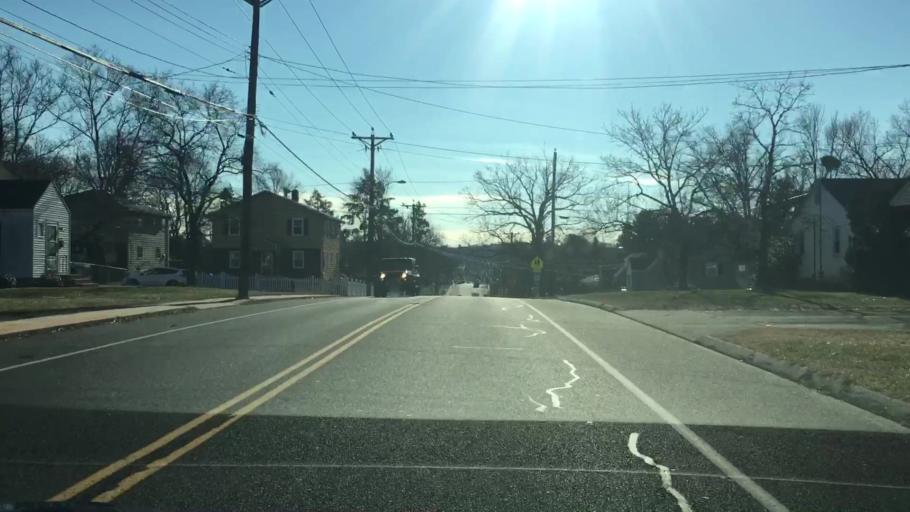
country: US
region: Connecticut
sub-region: Hartford County
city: Manchester
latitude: 41.7861
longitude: -72.5359
